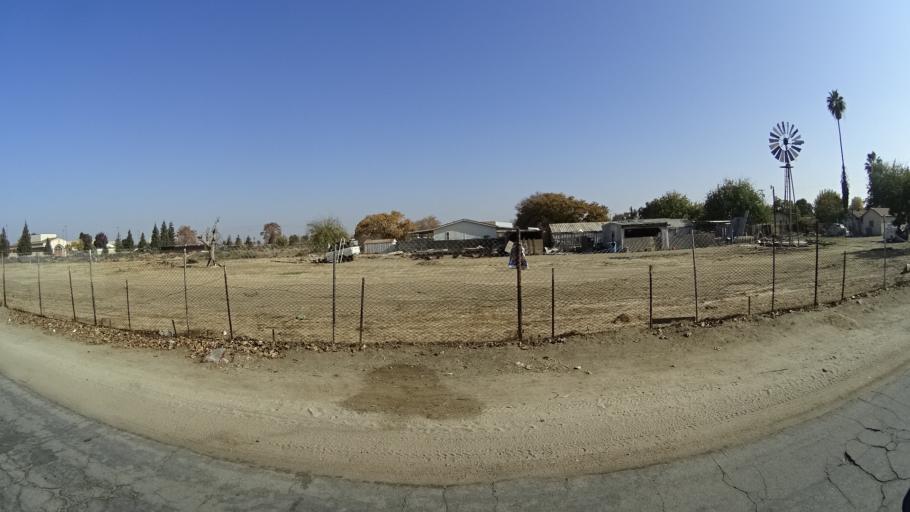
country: US
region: California
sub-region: Kern County
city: Greenfield
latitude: 35.2768
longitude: -119.0121
